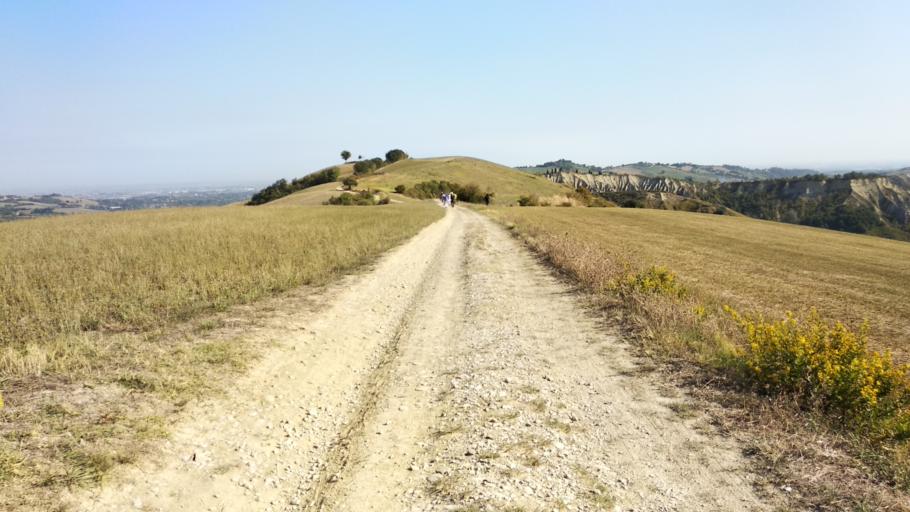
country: IT
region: Emilia-Romagna
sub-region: Provincia di Bologna
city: Borgo Tossignano
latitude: 44.3346
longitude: 11.5671
